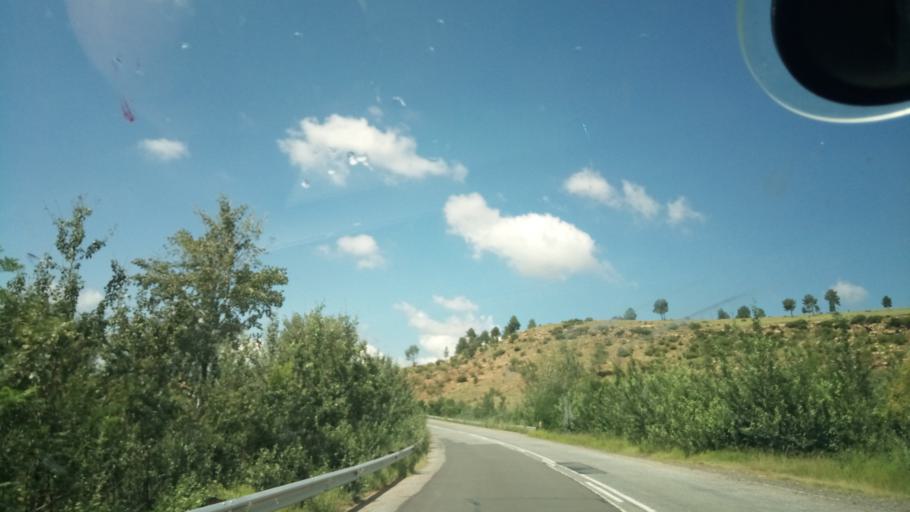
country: ZA
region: Orange Free State
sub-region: Thabo Mofutsanyana District Municipality
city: Ficksburg
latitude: -28.8778
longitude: 27.8656
